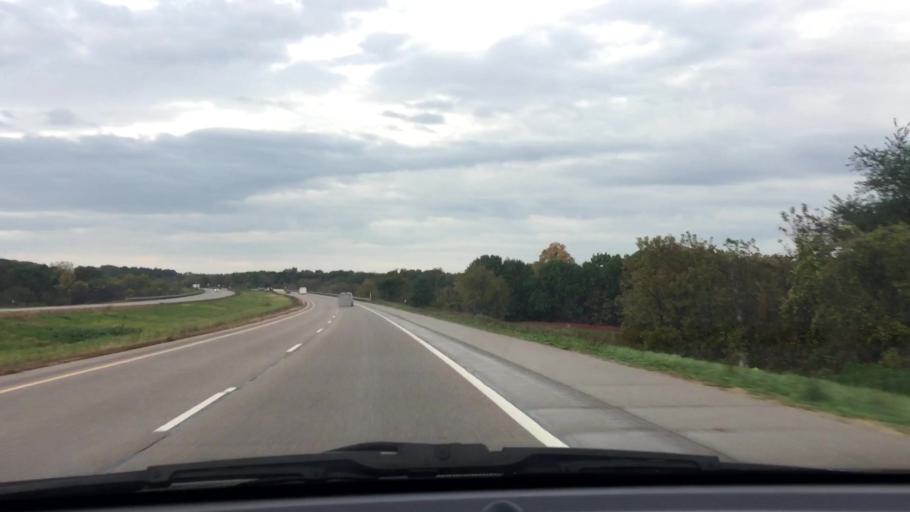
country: US
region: Wisconsin
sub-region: Rock County
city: Clinton
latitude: 42.5727
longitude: -88.8962
